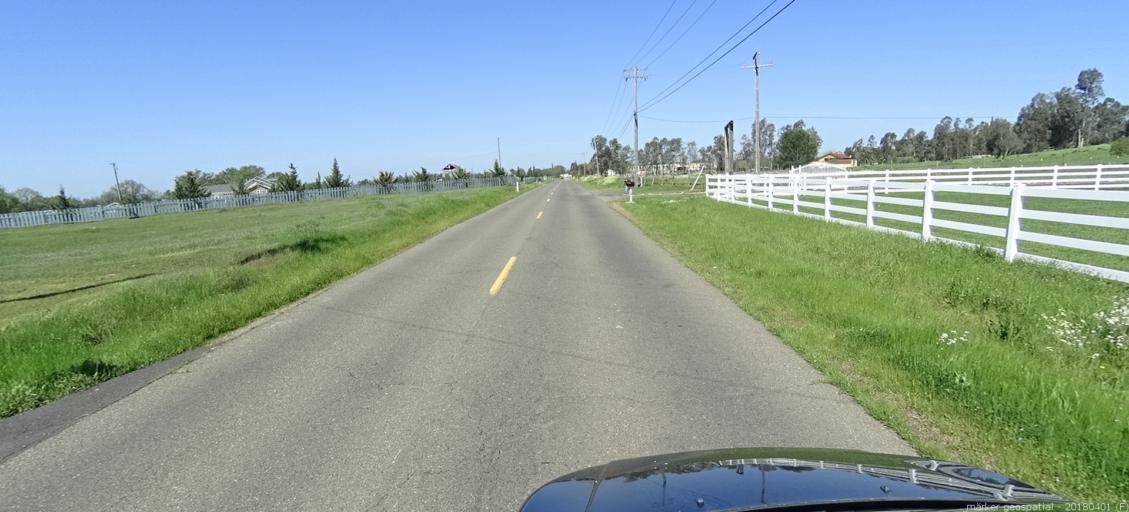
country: US
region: California
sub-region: Sacramento County
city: Wilton
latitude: 38.3998
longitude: -121.2442
